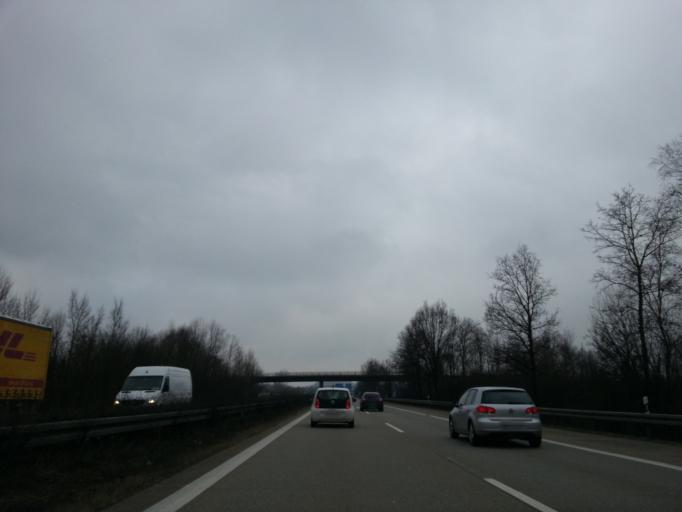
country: DE
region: Bavaria
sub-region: Lower Bavaria
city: Deggendorf
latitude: 48.8151
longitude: 12.9527
